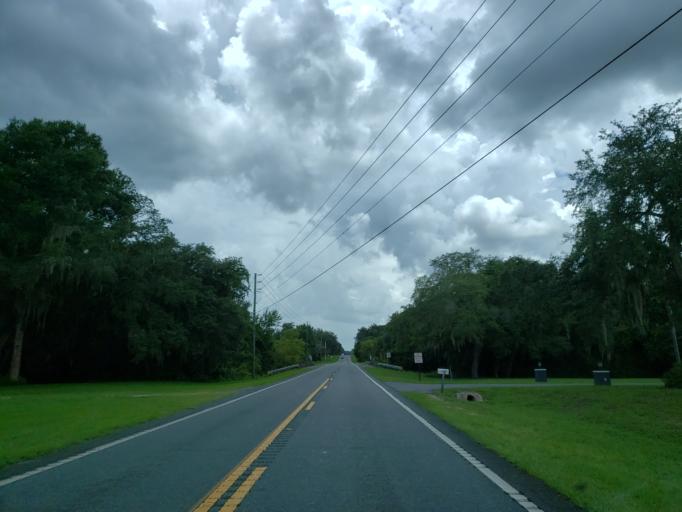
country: US
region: Florida
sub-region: Sumter County
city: Bushnell
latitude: 28.6401
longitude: -82.2210
